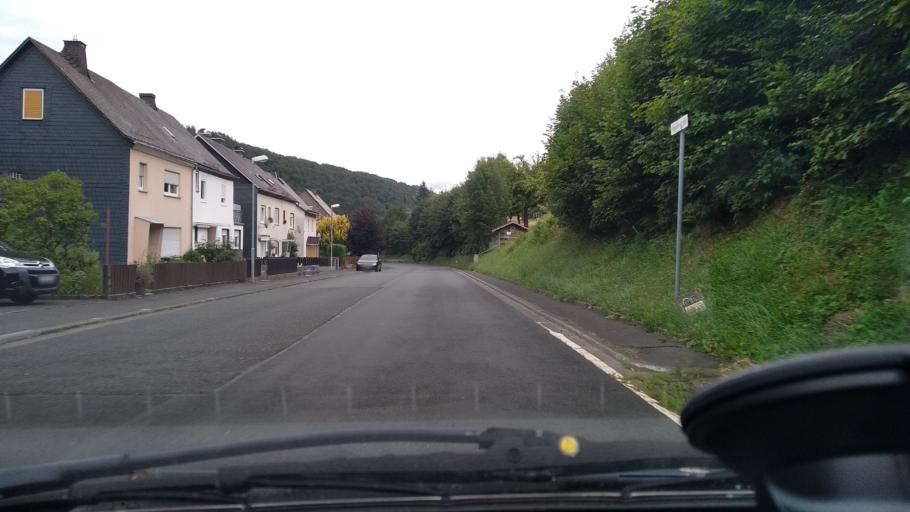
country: DE
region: Hesse
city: Dillenburg
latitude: 50.8460
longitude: 8.2766
